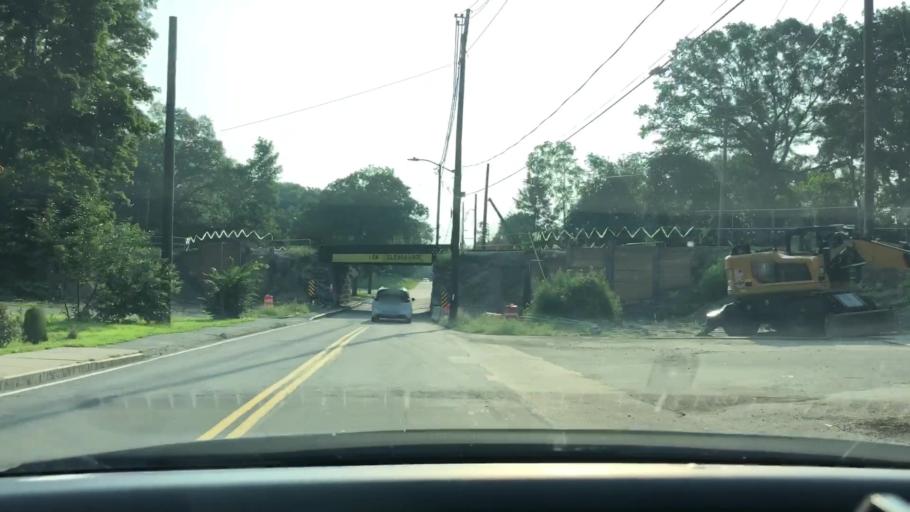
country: US
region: Massachusetts
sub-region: Norfolk County
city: Norwood
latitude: 42.2191
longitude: -71.1862
